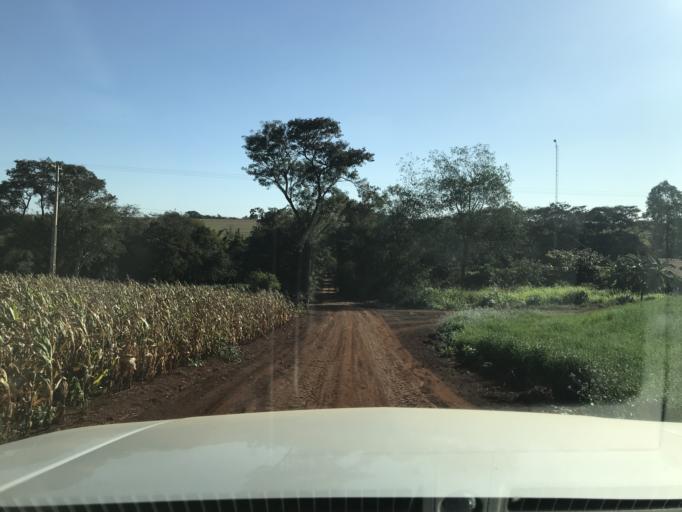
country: BR
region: Parana
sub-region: Palotina
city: Palotina
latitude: -24.2273
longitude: -53.8127
